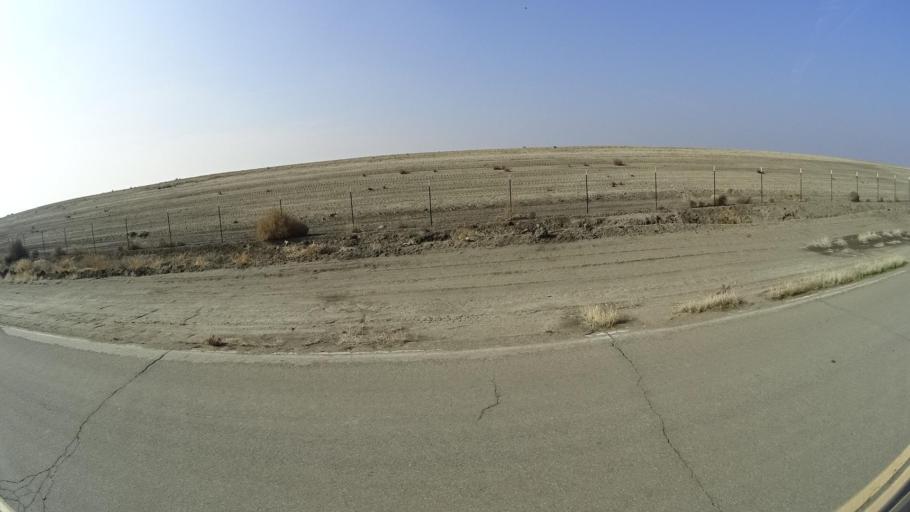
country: US
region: California
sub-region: Kern County
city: Buttonwillow
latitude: 35.3381
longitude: -119.3767
